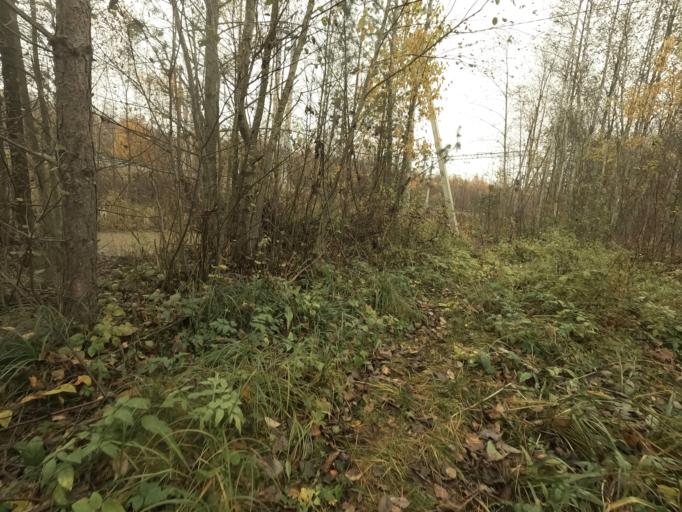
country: RU
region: Leningrad
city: Pavlovo
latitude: 59.7903
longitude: 30.8822
